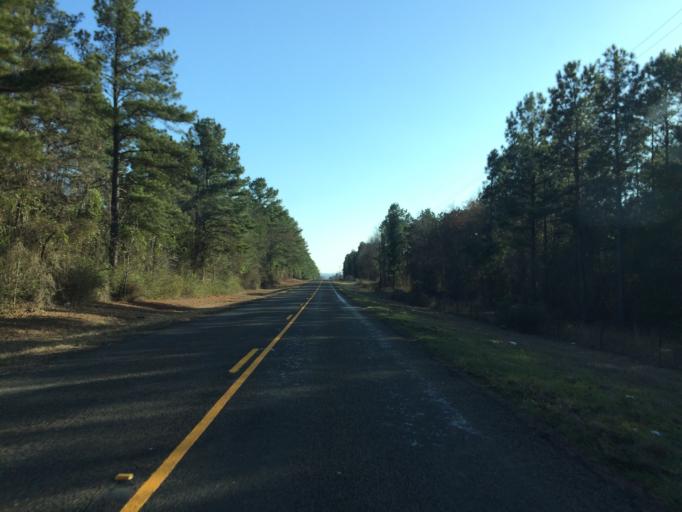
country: US
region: Texas
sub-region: Wood County
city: Hawkins
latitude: 32.6300
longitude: -95.3132
